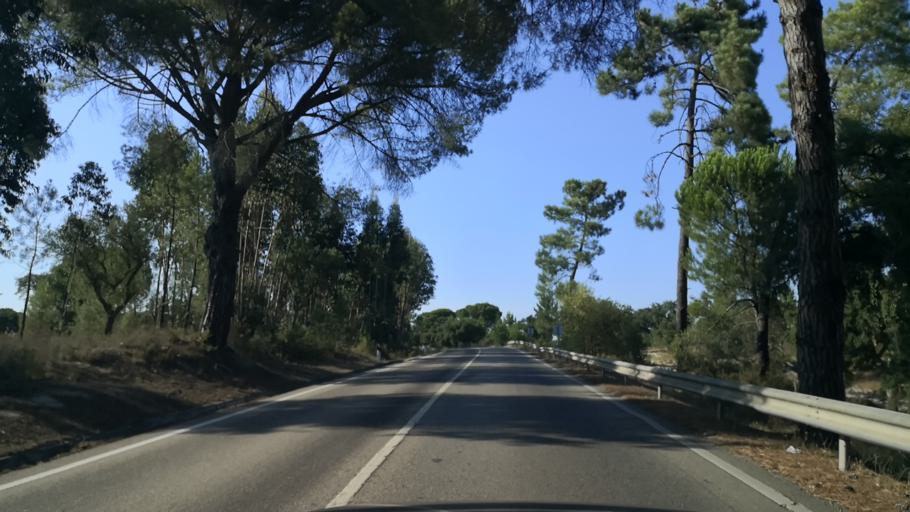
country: PT
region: Santarem
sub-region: Coruche
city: Coruche
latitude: 38.9726
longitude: -8.5385
